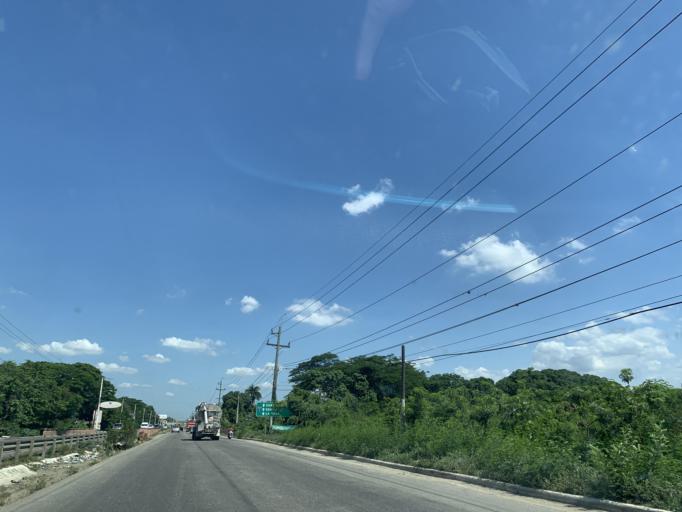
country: DO
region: Santiago
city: Villa Gonzalez
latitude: 19.5238
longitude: -70.7693
